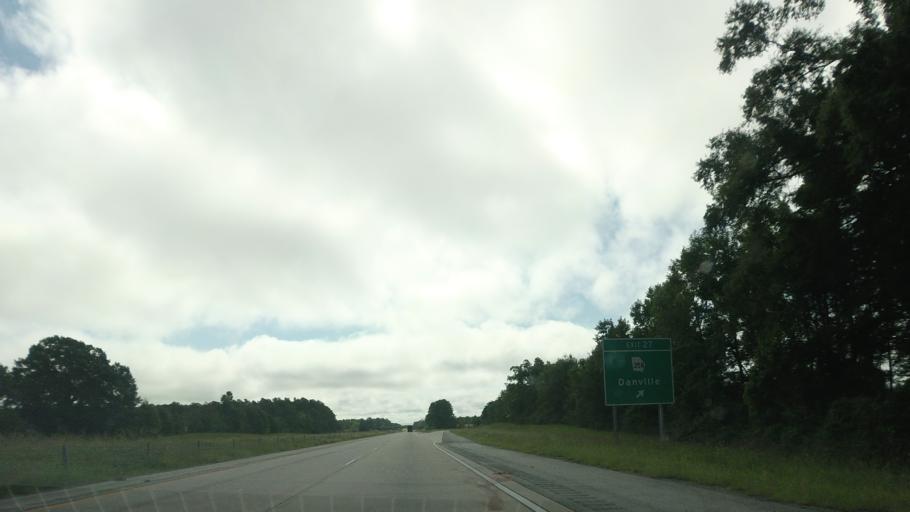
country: US
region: Georgia
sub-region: Twiggs County
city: Jeffersonville
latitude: 32.6016
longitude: -83.3193
